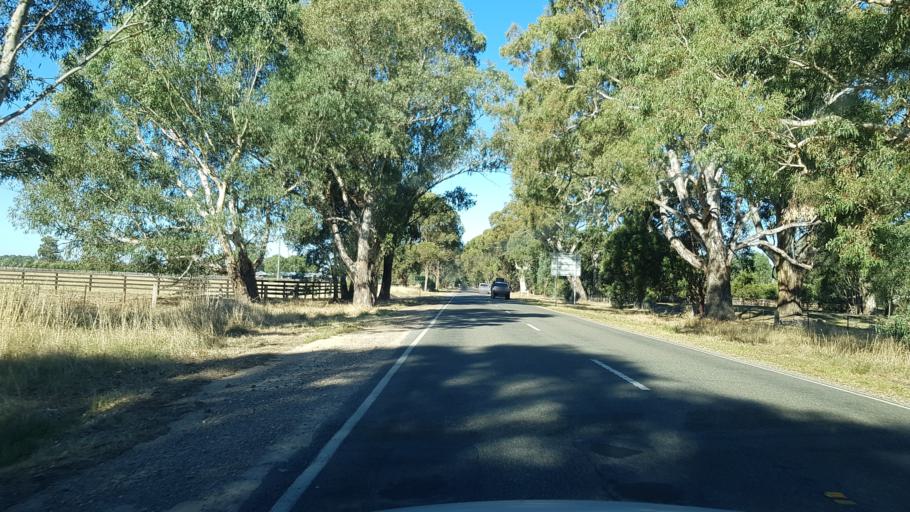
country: AU
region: Victoria
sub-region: Wangaratta
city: Wangaratta
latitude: -36.4323
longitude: 146.2933
